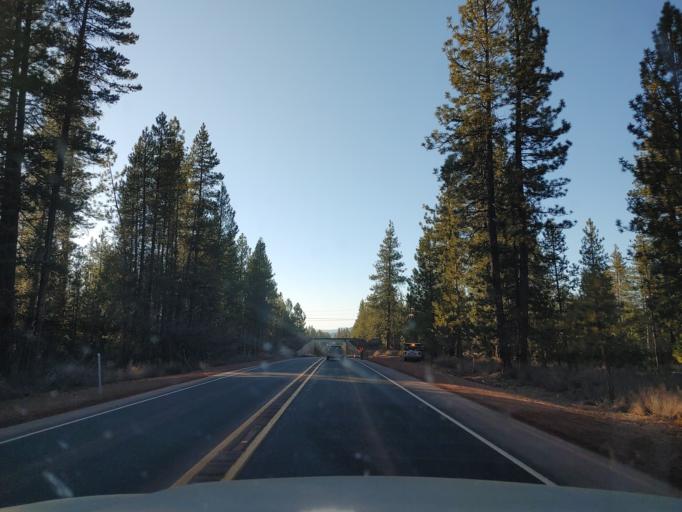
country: US
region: Oregon
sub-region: Deschutes County
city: La Pine
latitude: 43.3758
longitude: -121.7965
